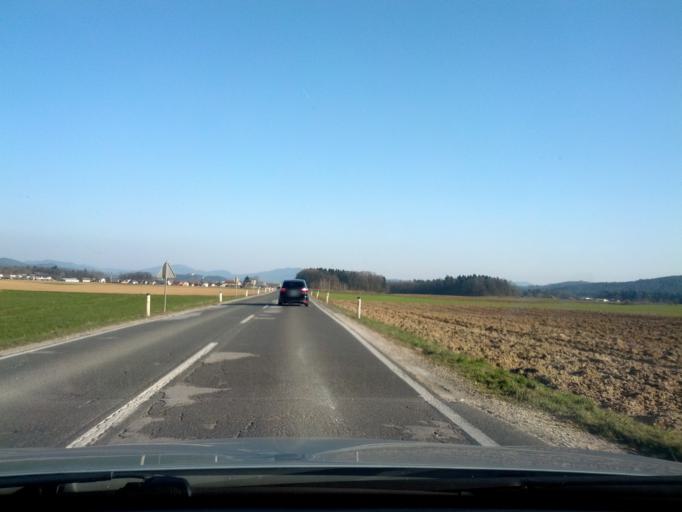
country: SI
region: Komenda
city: Komenda
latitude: 46.2046
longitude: 14.5253
